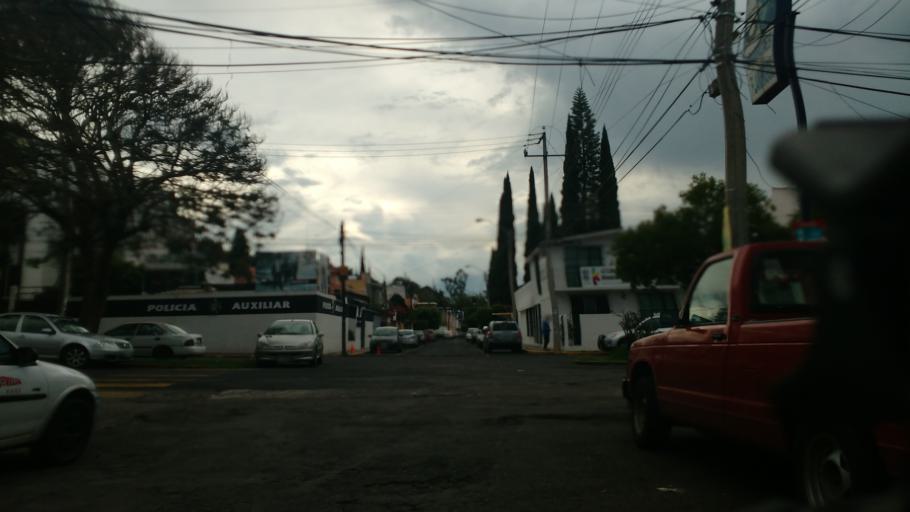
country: MX
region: Michoacan
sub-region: Morelia
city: Montana Monarca (Punta Altozano)
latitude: 19.6811
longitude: -101.1740
